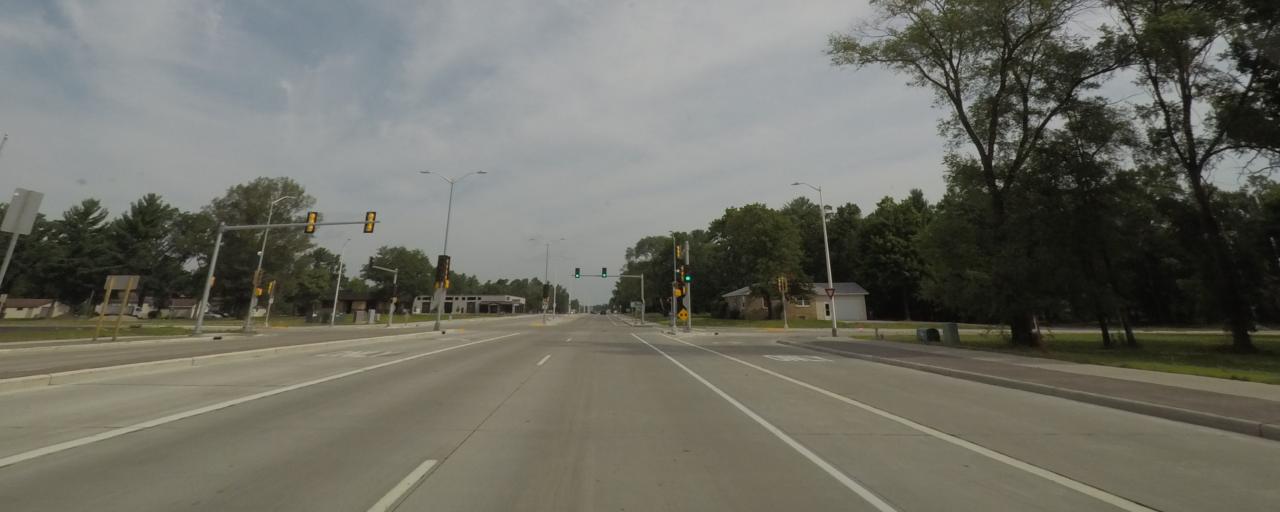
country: US
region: Wisconsin
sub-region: Portage County
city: Whiting
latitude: 44.4811
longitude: -89.5492
